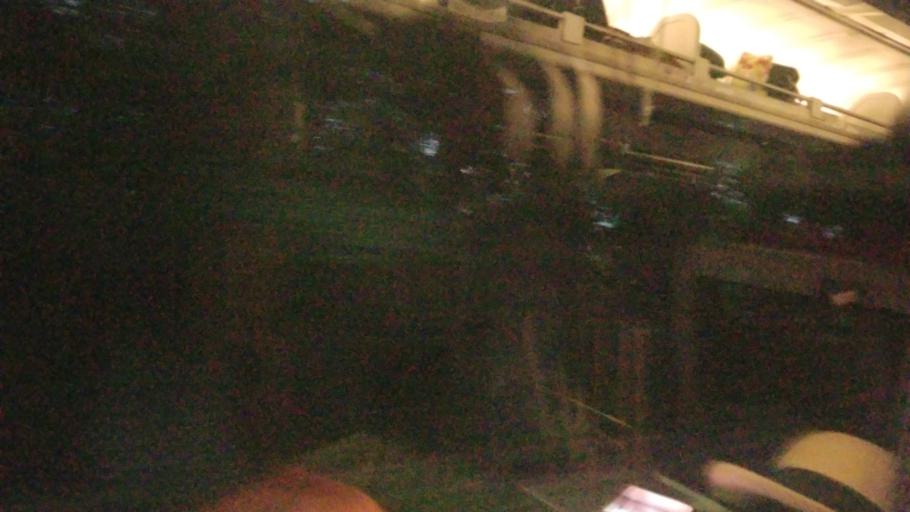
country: US
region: Virginia
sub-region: Orange County
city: Gordonsville
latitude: 38.1853
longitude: -78.2535
